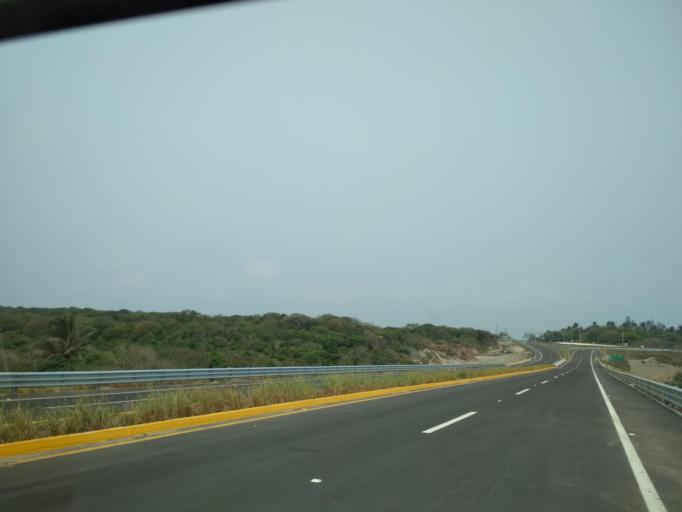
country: MX
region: Veracruz
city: Anton Lizardo
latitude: 19.0503
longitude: -96.0047
